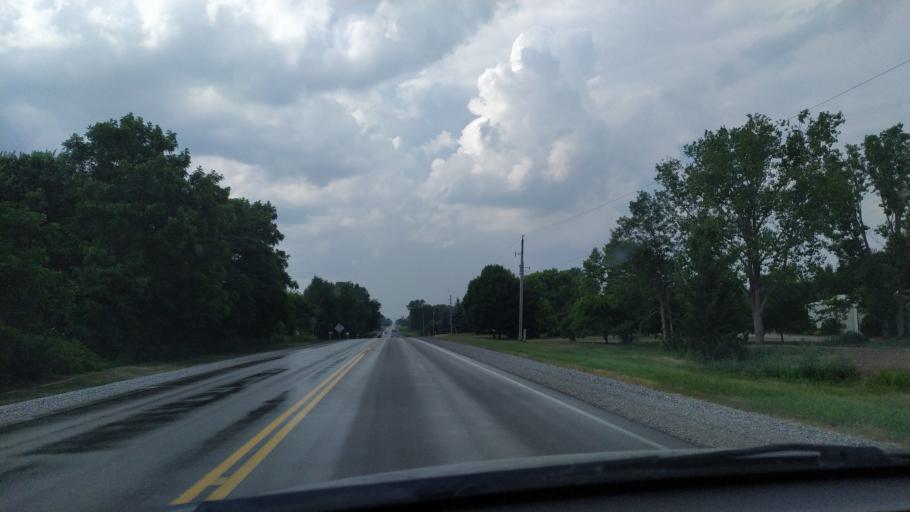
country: CA
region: Ontario
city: Dorchester
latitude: 43.0870
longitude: -81.1492
